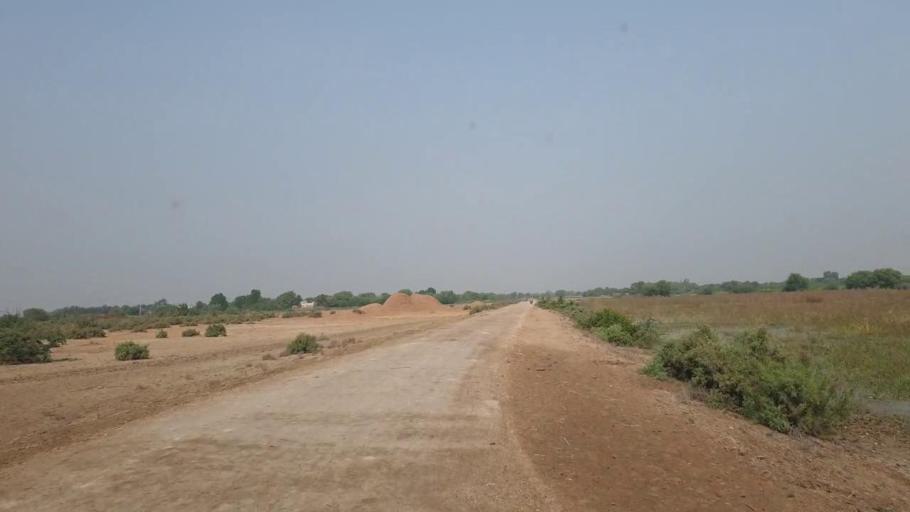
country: PK
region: Sindh
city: Matli
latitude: 25.1578
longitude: 68.7295
